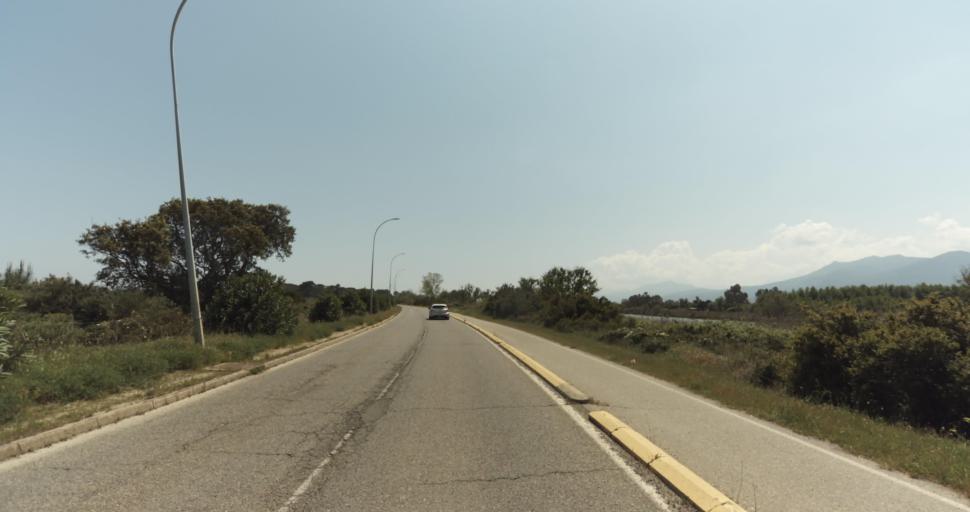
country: FR
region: Corsica
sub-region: Departement de la Haute-Corse
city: Biguglia
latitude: 42.6528
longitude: 9.4505
